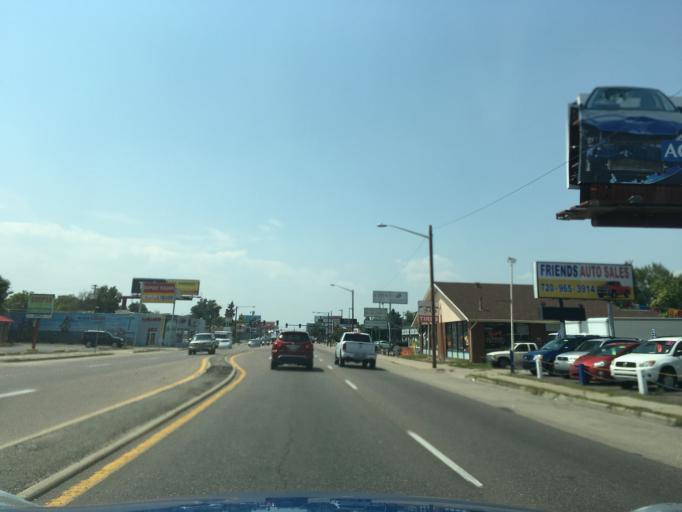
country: US
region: Colorado
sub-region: Arapahoe County
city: Glendale
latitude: 39.7402
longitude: -104.8964
